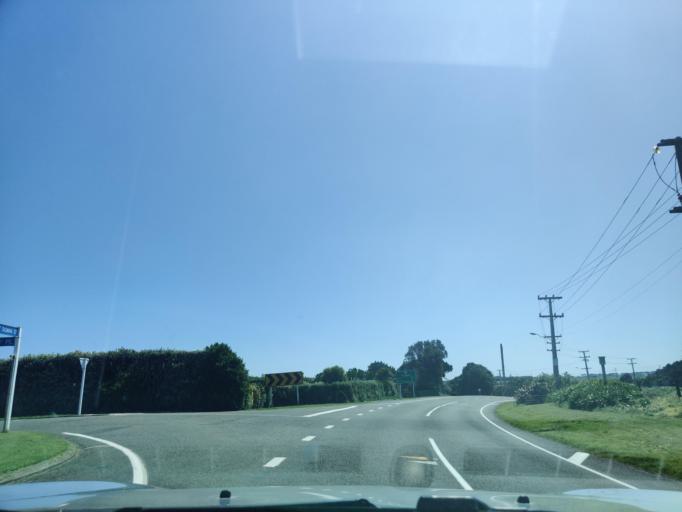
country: NZ
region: Taranaki
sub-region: South Taranaki District
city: Opunake
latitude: -39.4491
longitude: 173.8465
